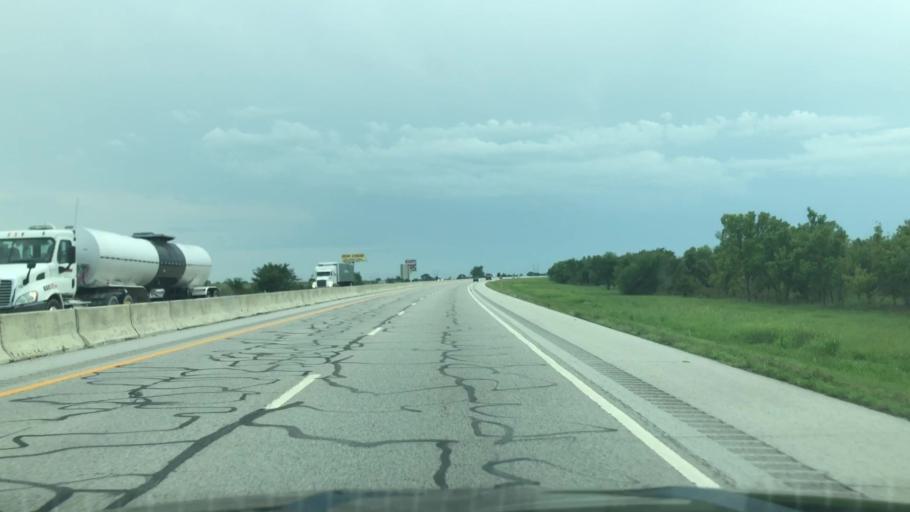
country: US
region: Oklahoma
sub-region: Craig County
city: Vinita
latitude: 36.5536
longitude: -95.2232
